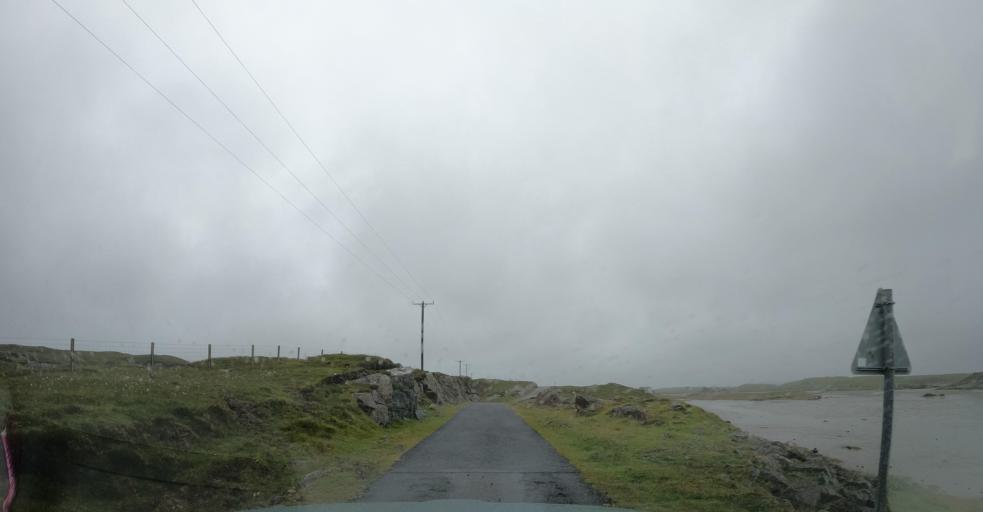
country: GB
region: Scotland
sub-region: Eilean Siar
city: Benbecula
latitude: 57.4970
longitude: -7.2394
